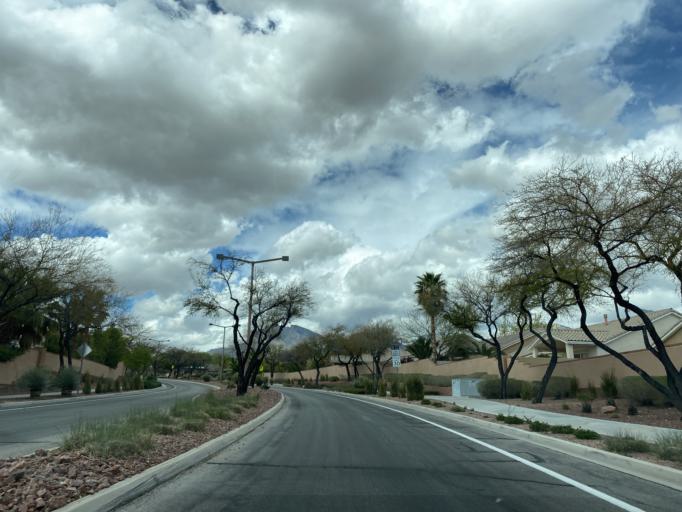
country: US
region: Nevada
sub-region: Clark County
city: Summerlin South
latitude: 36.1900
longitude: -115.3307
